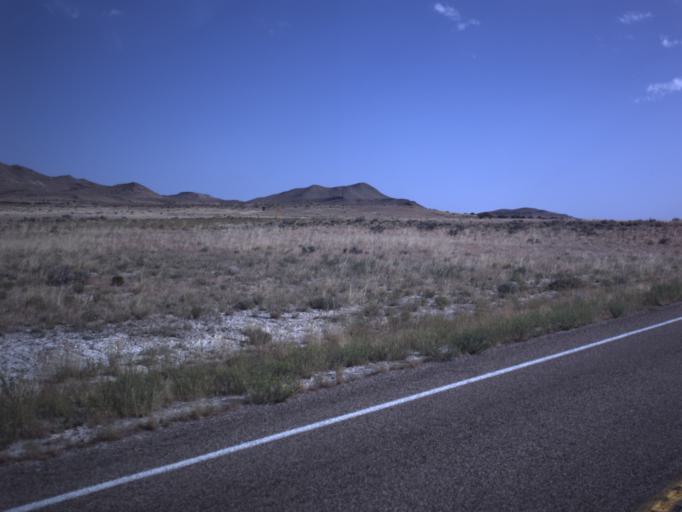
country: US
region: Utah
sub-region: Beaver County
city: Milford
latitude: 38.8260
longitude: -112.8514
